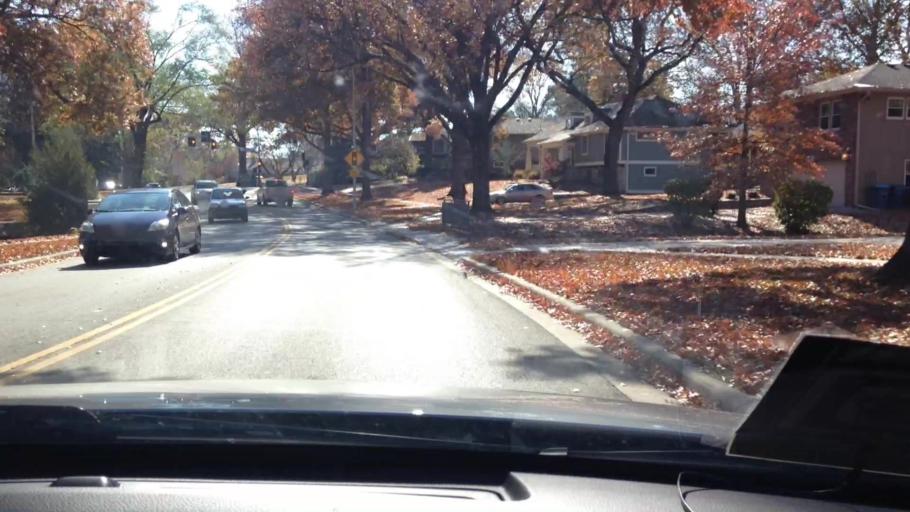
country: US
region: Kansas
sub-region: Johnson County
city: Prairie Village
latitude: 38.9799
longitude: -94.6395
